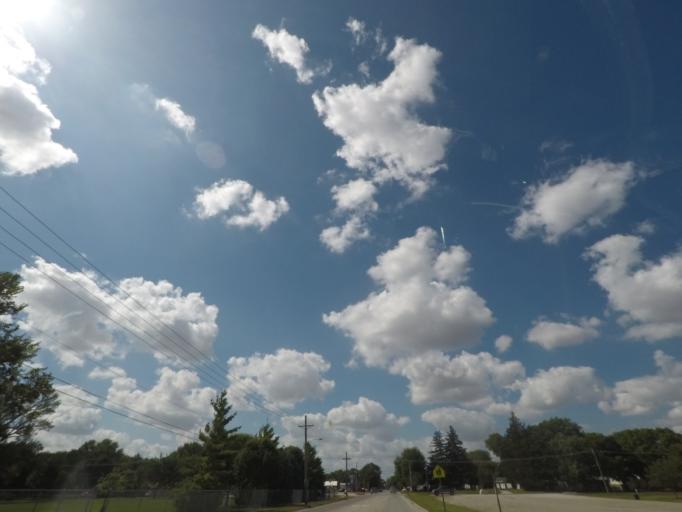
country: US
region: Iowa
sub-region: Story County
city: Nevada
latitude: 42.0228
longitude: -93.4385
